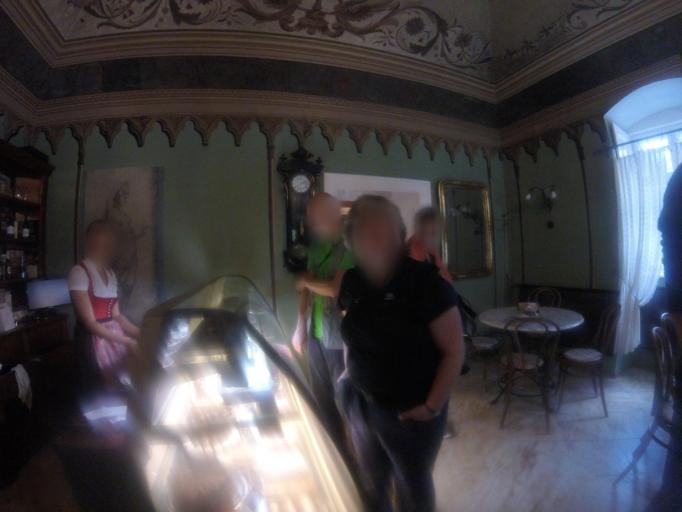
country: HU
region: Bekes
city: Gyula
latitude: 46.6463
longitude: 21.2744
